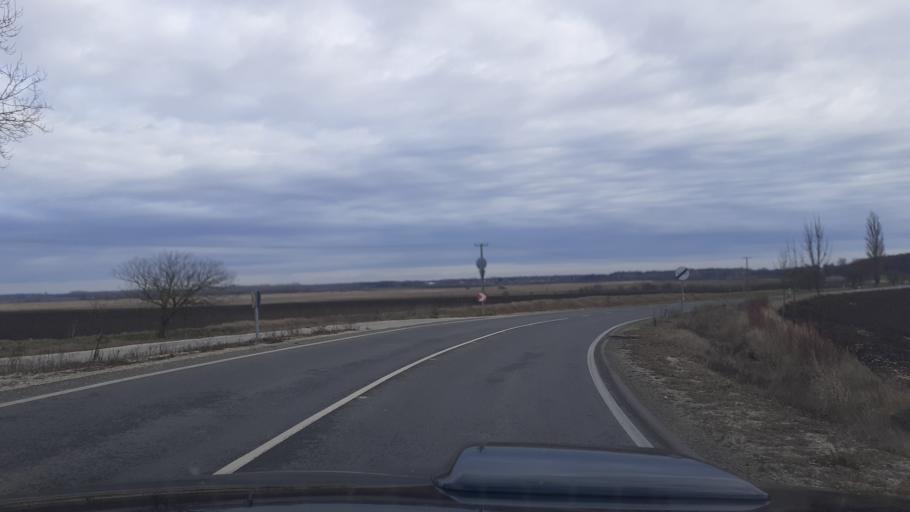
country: HU
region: Fejer
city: Seregelyes
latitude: 47.1288
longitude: 18.5483
